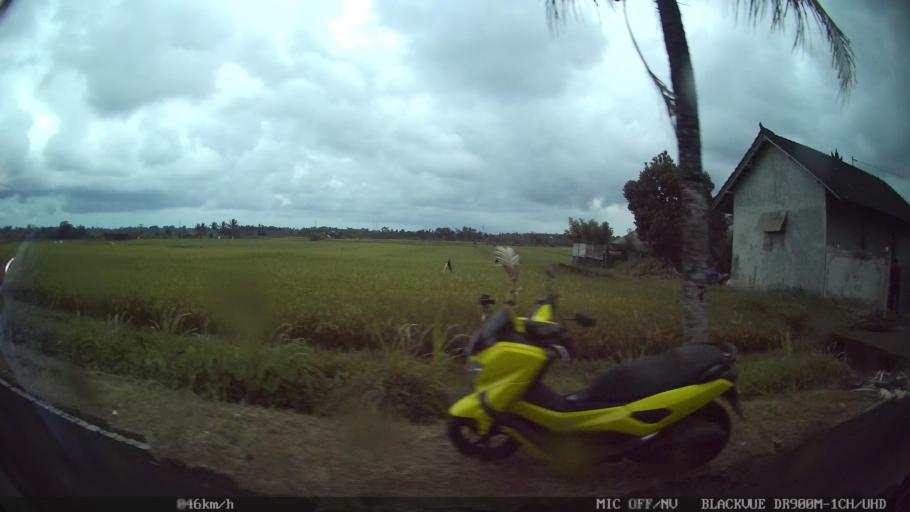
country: ID
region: Bali
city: Banjar Cemenggon
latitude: -8.5326
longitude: 115.1891
